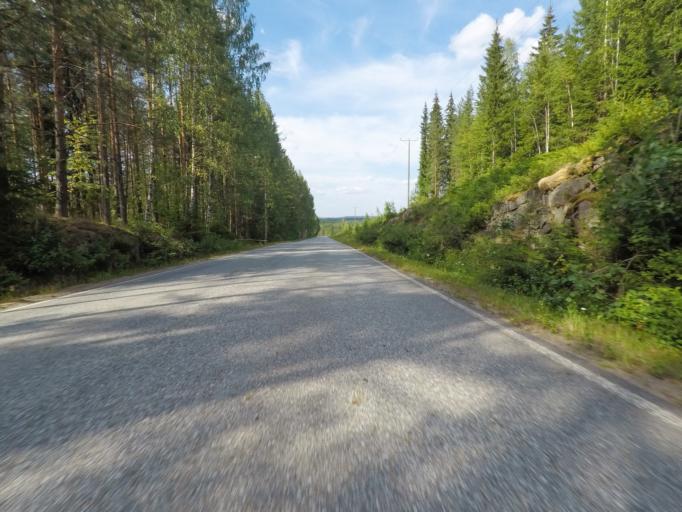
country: FI
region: Southern Savonia
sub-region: Savonlinna
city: Sulkava
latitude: 61.7123
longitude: 28.2102
